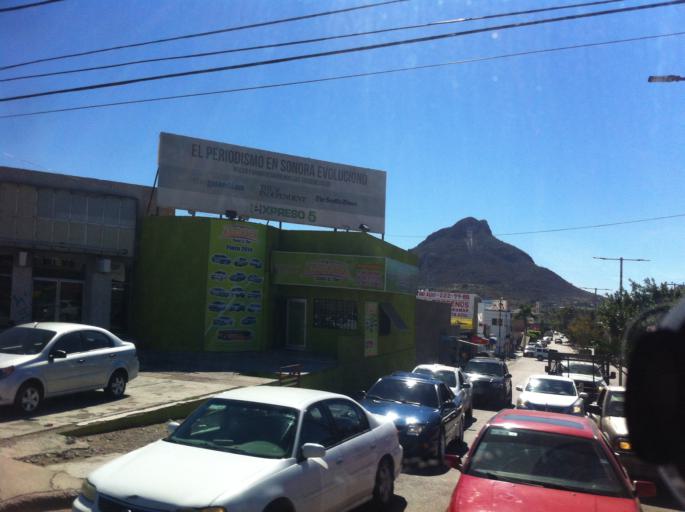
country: MX
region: Sonora
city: Heroica Guaymas
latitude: 27.9256
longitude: -110.9181
